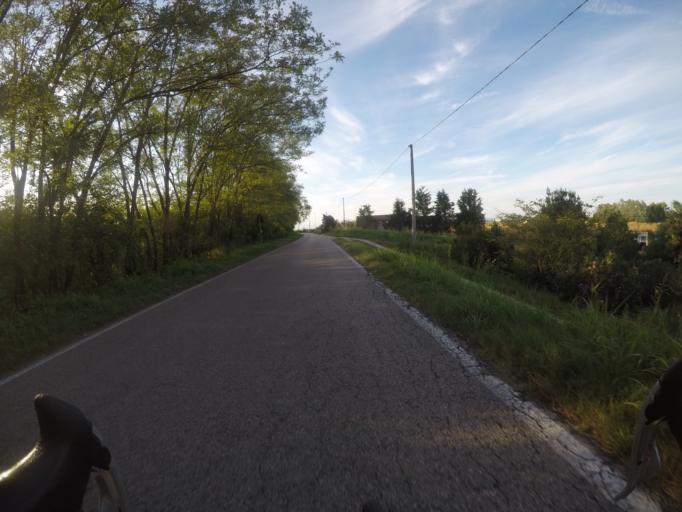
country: IT
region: Veneto
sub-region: Provincia di Rovigo
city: San Bellino
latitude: 45.0154
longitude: 11.5656
